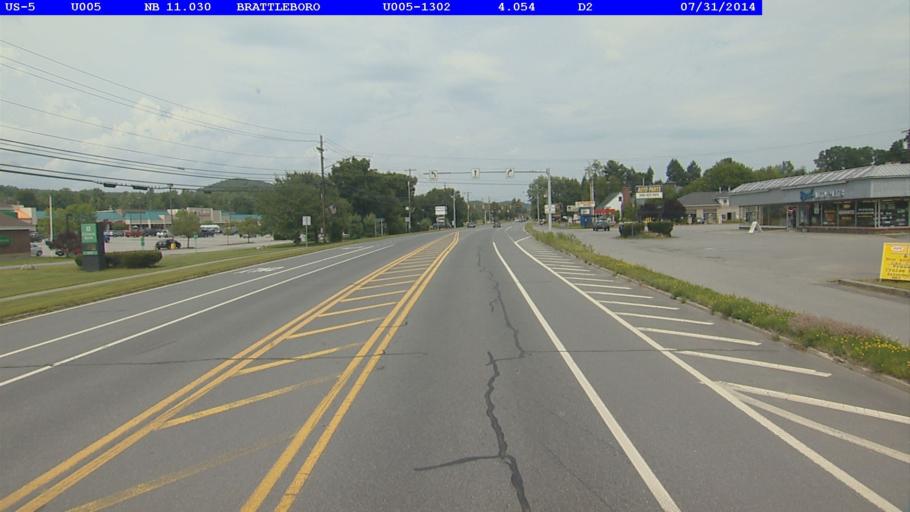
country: US
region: Vermont
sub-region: Windham County
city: Brattleboro
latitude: 42.8772
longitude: -72.5601
